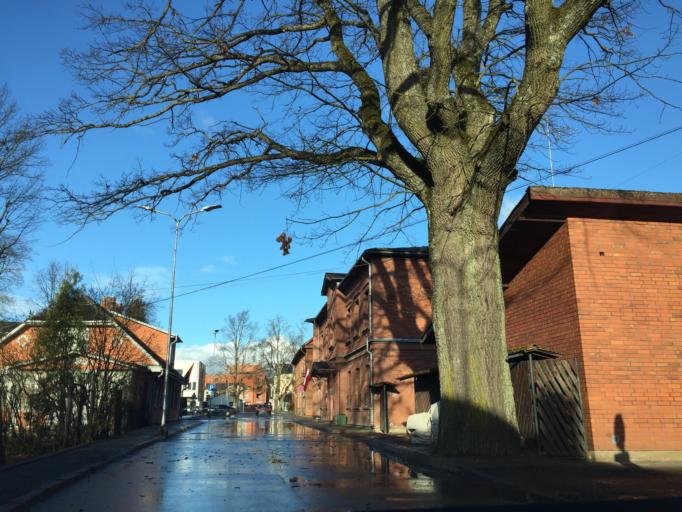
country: LV
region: Valmieras Rajons
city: Valmiera
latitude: 57.5357
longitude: 25.4155
